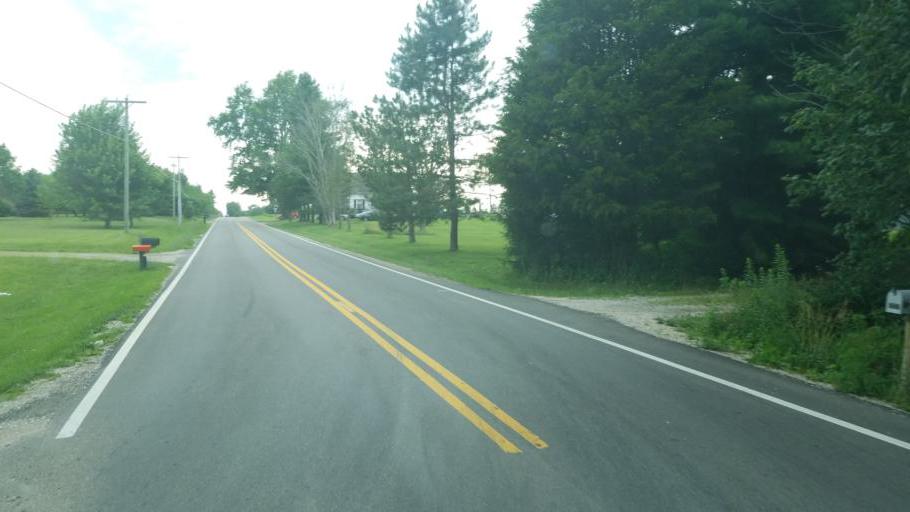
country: US
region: Ohio
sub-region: Delaware County
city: Ashley
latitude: 40.3336
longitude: -82.9180
